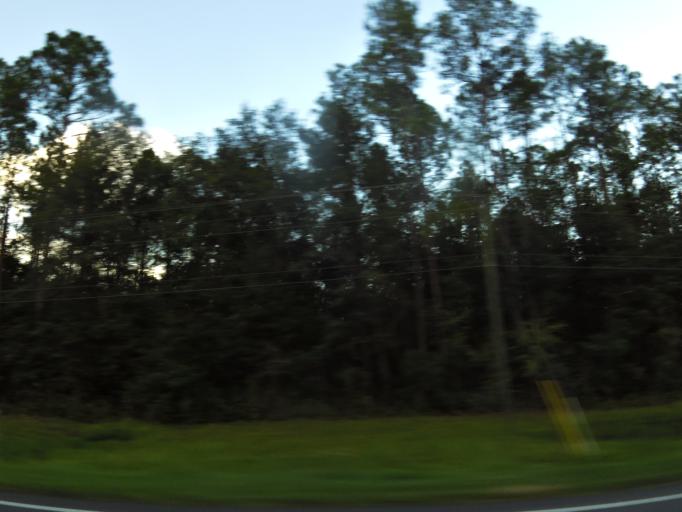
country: US
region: Georgia
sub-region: Echols County
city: Statenville
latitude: 30.7090
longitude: -83.0567
